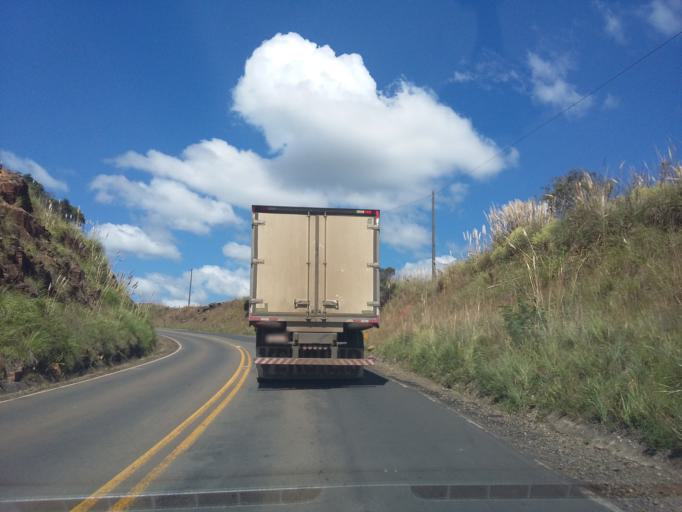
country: BR
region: Santa Catarina
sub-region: Sao Joaquim
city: Sao Joaquim
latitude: -28.3160
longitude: -49.7124
